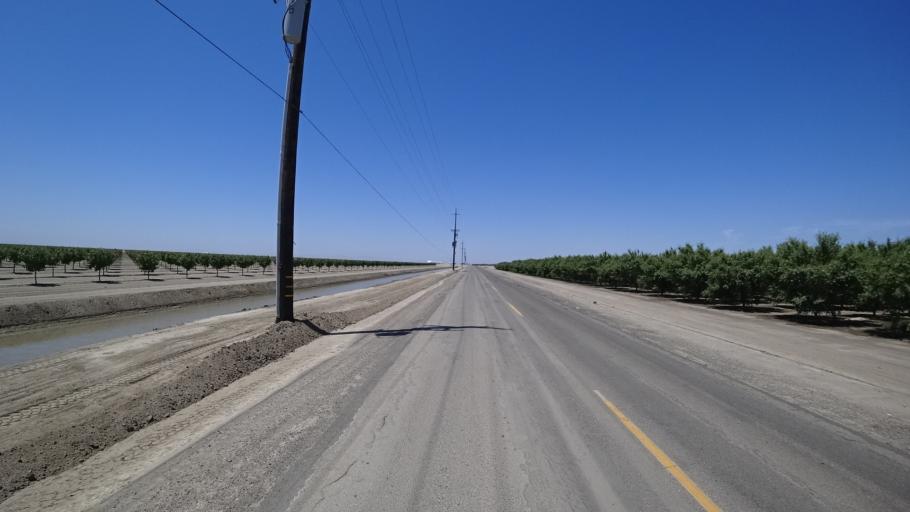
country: US
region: California
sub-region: Kings County
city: Corcoran
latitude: 36.1090
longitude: -119.6041
